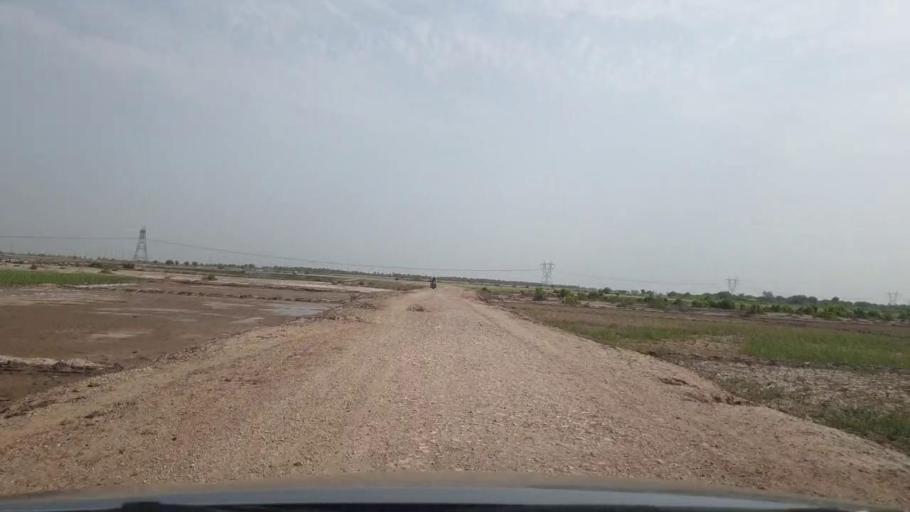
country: PK
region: Sindh
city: Rohri
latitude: 27.6687
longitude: 69.0258
